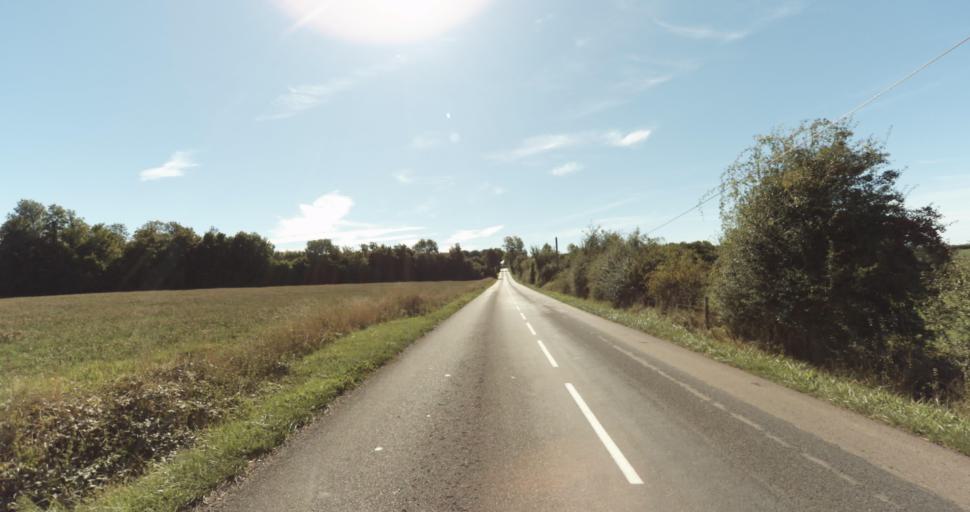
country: FR
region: Lower Normandy
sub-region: Departement de l'Orne
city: Gace
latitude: 48.7937
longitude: 0.2175
